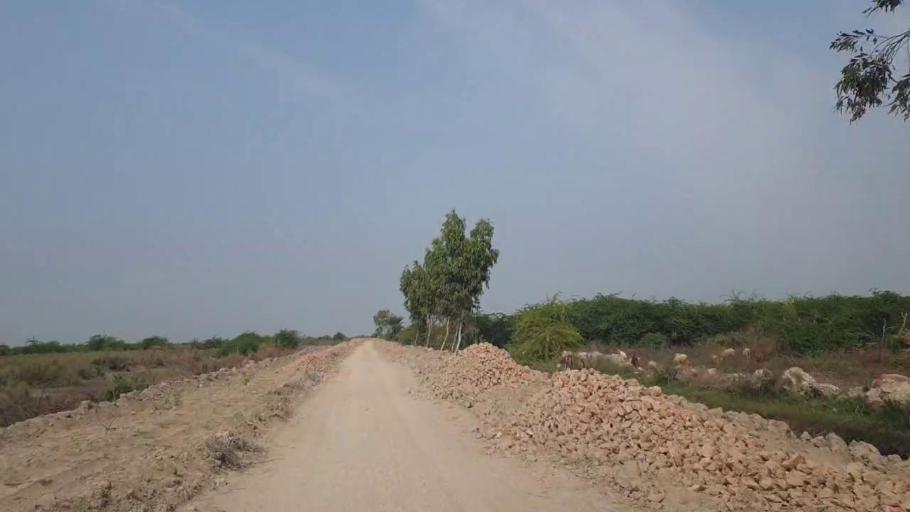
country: PK
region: Sindh
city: Badin
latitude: 24.6040
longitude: 68.7416
